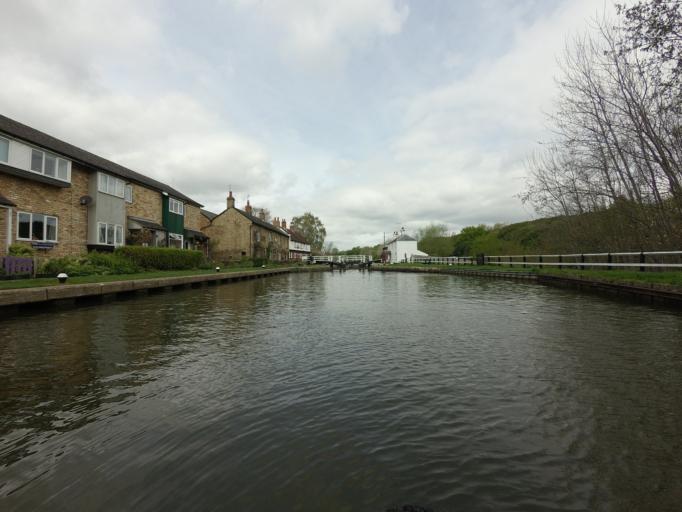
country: GB
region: England
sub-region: Milton Keynes
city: Water Eaton
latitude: 52.0002
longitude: -0.7141
